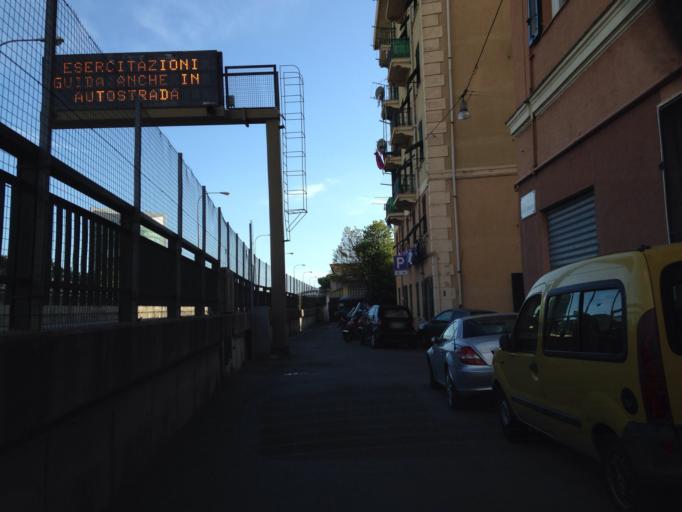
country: IT
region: Liguria
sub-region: Provincia di Genova
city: San Teodoro
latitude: 44.4188
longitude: 8.8818
